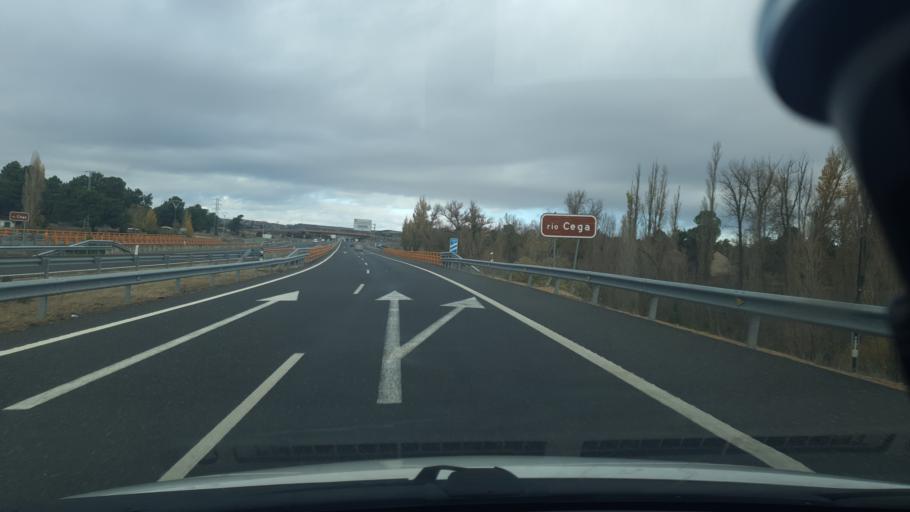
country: ES
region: Castille and Leon
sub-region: Provincia de Segovia
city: Sanchonuno
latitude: 41.3635
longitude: -4.2984
